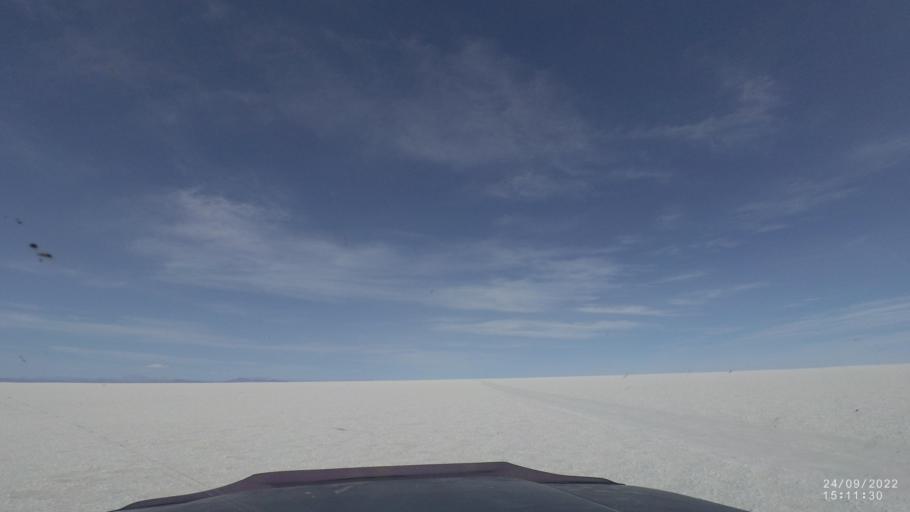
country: BO
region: Potosi
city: Colchani
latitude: -19.9452
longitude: -67.4766
